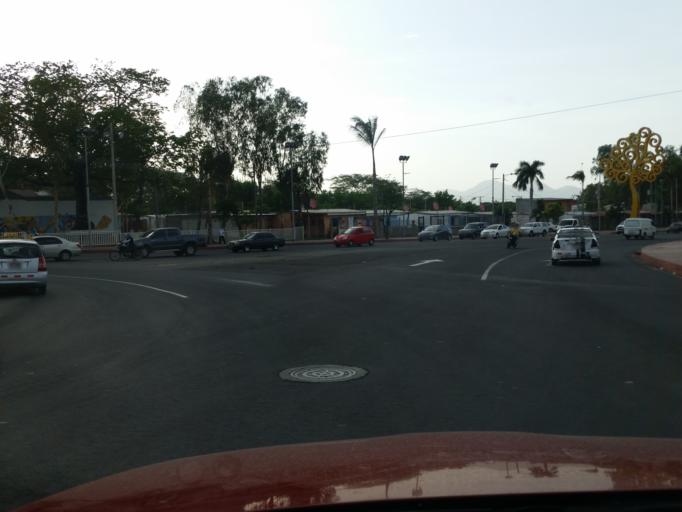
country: NI
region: Managua
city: Managua
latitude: 12.1462
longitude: -86.2744
